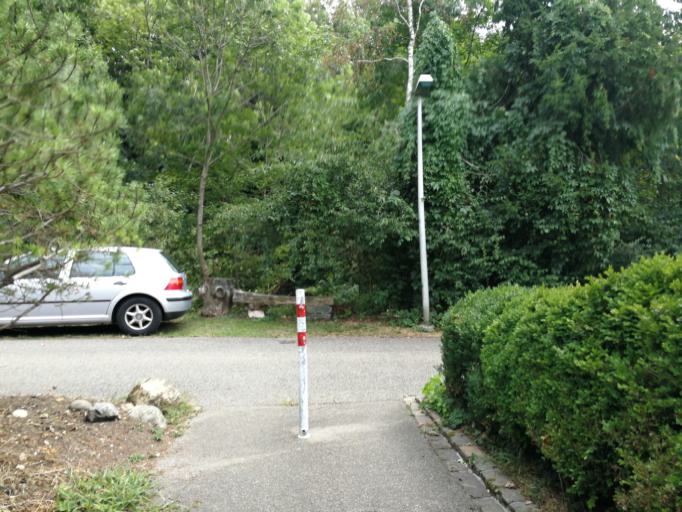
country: CH
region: Zurich
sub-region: Bezirk Meilen
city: Feldmeilen
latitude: 47.2844
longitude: 8.6254
